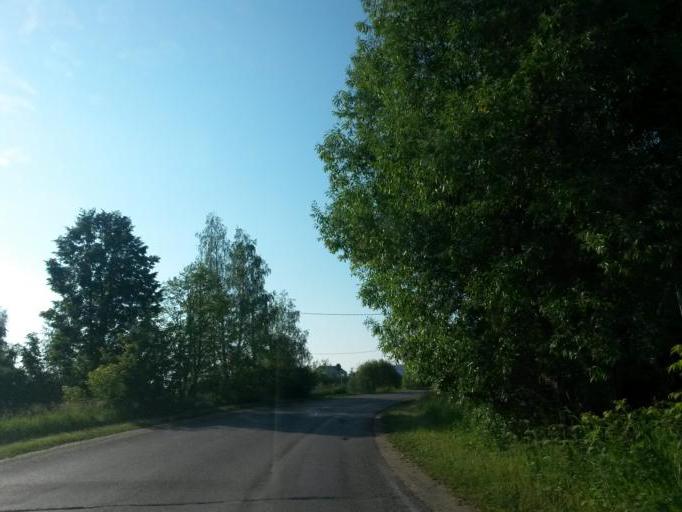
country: RU
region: Moskovskaya
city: Lyubuchany
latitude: 55.2479
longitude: 37.6387
